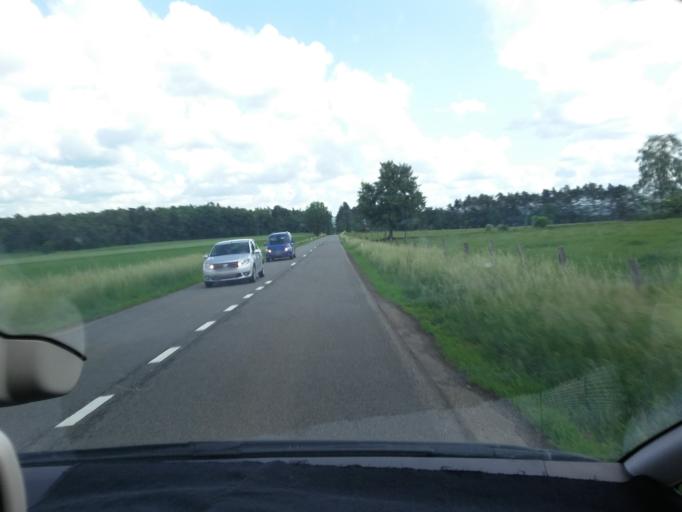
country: BE
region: Wallonia
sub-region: Province de Namur
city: Rochefort
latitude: 50.1362
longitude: 5.2277
